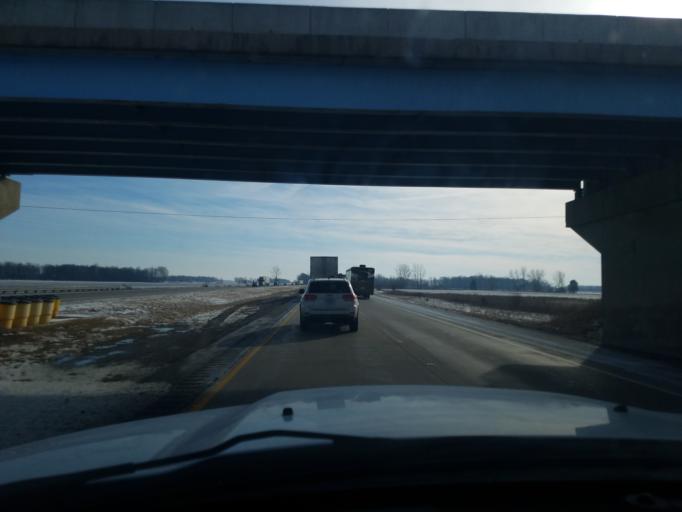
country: US
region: Indiana
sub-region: Huntington County
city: Markle
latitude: 40.7858
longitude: -85.3838
